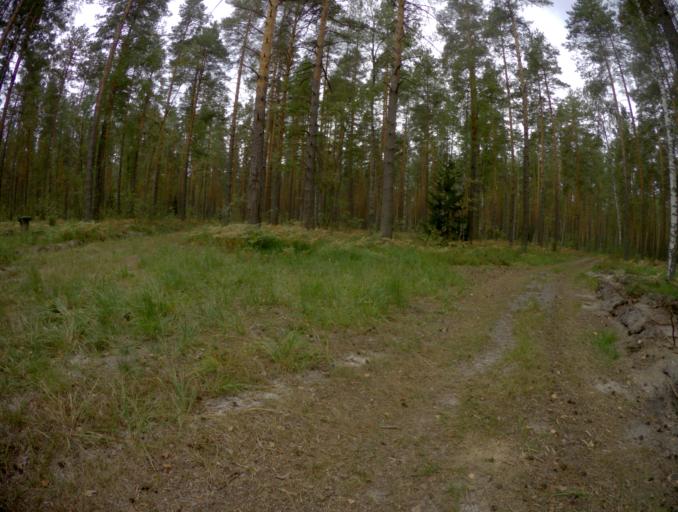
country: RU
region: Vladimir
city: Ivanishchi
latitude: 55.8320
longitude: 40.3114
